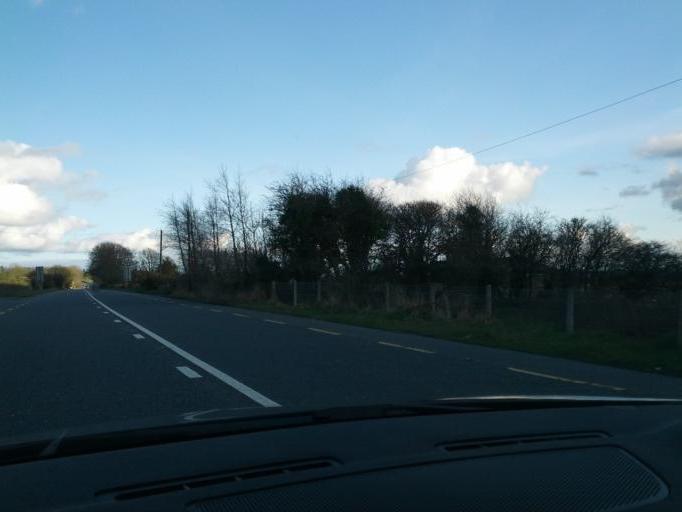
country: IE
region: Connaught
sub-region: Roscommon
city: Castlerea
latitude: 53.6849
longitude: -8.3621
